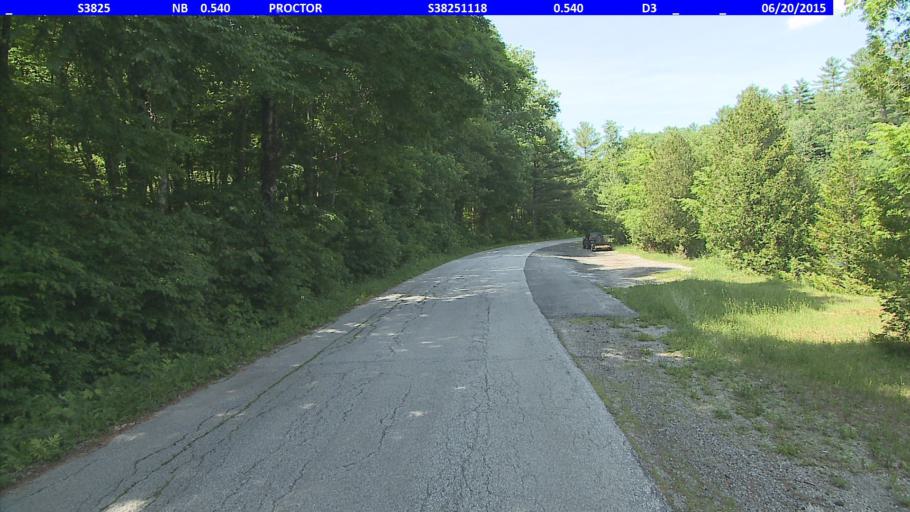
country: US
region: Vermont
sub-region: Rutland County
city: West Rutland
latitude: 43.6663
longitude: -73.0477
